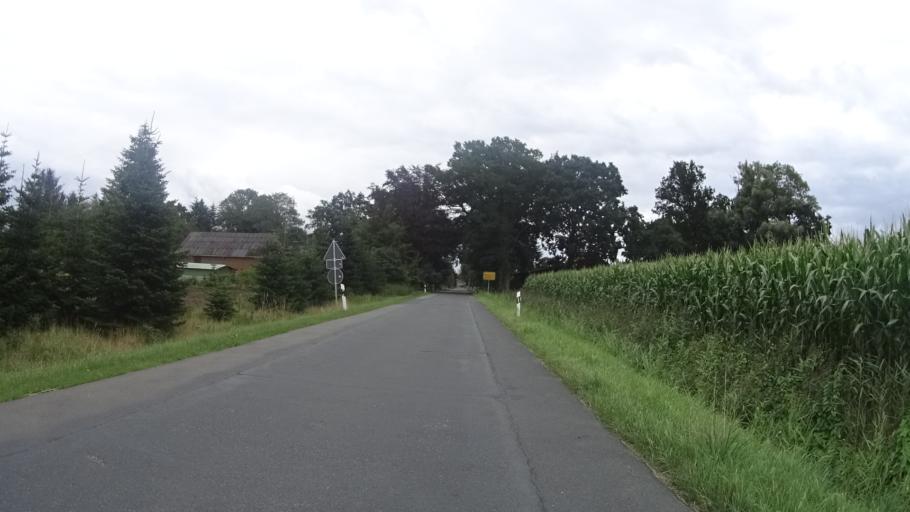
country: DE
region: Lower Saxony
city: Stinstedt
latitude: 53.6370
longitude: 8.9552
